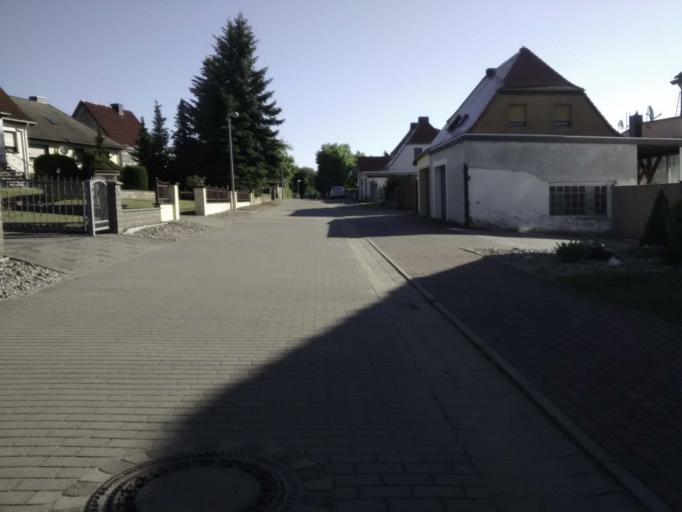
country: DE
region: Saxony-Anhalt
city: Rogatz
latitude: 52.3191
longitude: 11.7743
